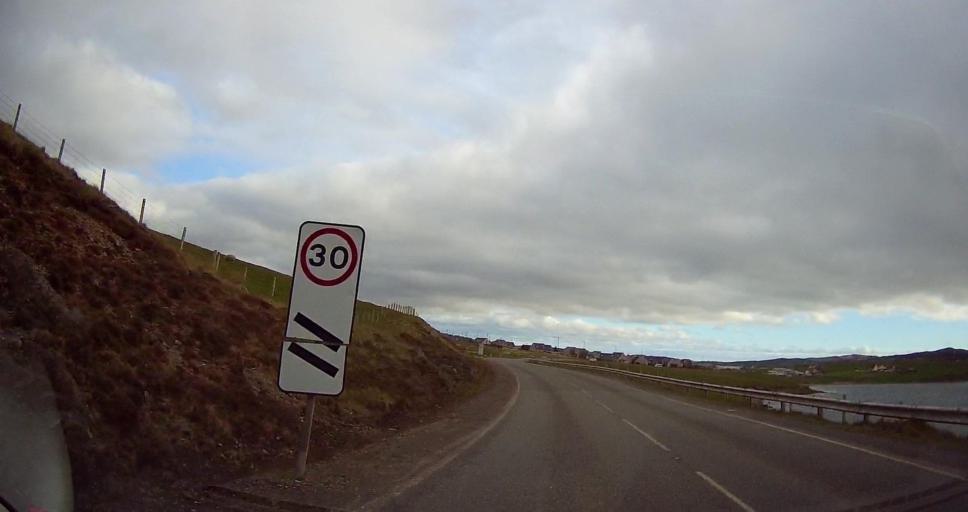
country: GB
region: Scotland
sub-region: Shetland Islands
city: Lerwick
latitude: 60.4038
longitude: -1.3489
